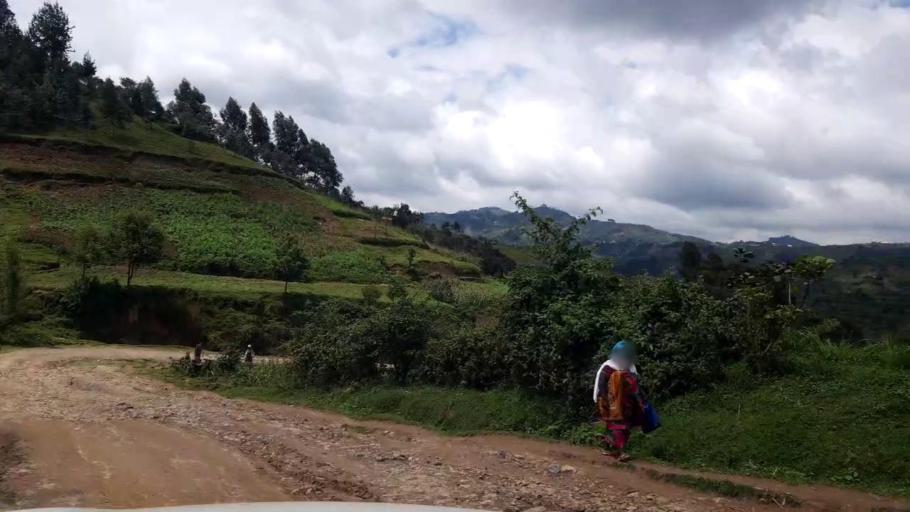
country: RW
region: Western Province
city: Kibuye
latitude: -1.9203
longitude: 29.4565
